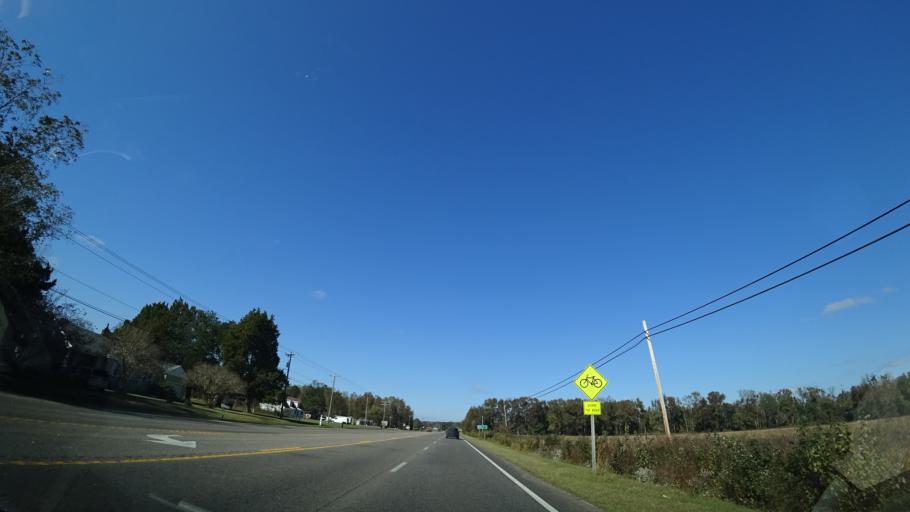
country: US
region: North Carolina
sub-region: Currituck County
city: Currituck
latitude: 36.2745
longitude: -75.9115
